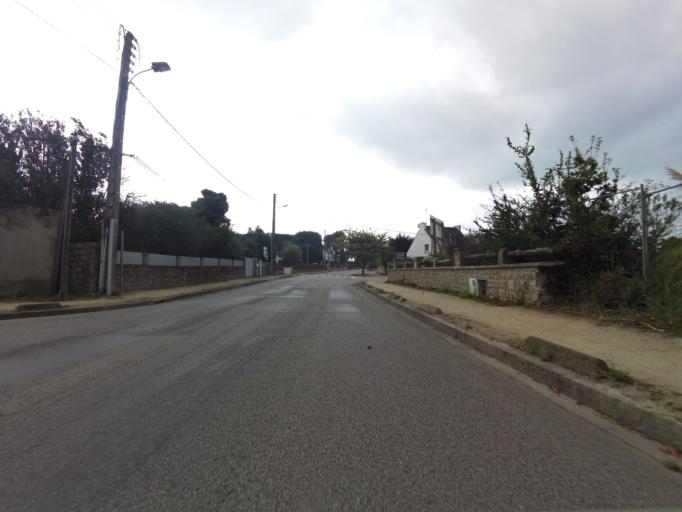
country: FR
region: Brittany
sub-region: Departement du Morbihan
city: Carnac
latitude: 47.5820
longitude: -3.0752
